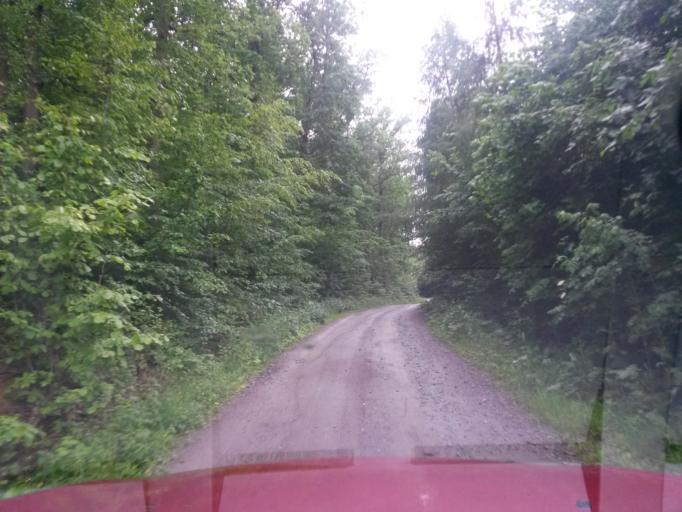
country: SK
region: Kosicky
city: Kosice
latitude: 48.7028
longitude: 21.1842
